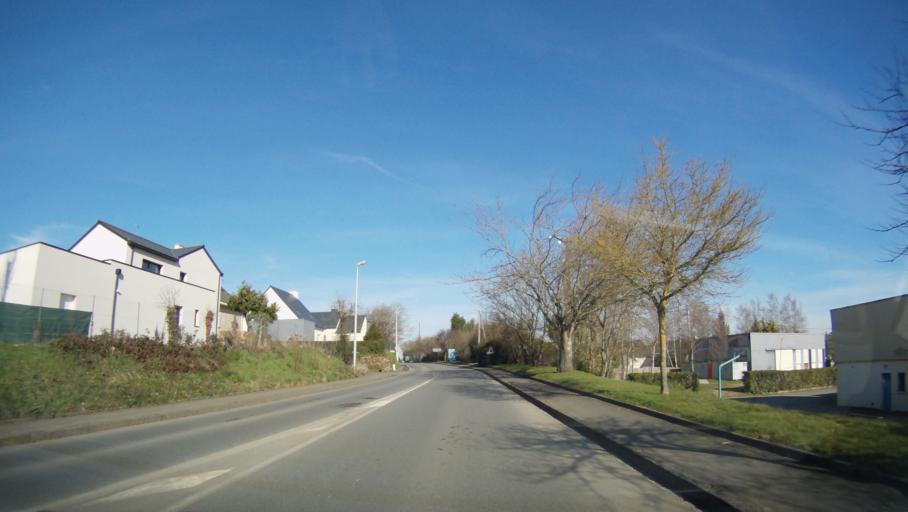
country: FR
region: Brittany
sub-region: Departement d'Ille-et-Vilaine
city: Saint-Erblon
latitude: 48.0224
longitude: -1.6540
